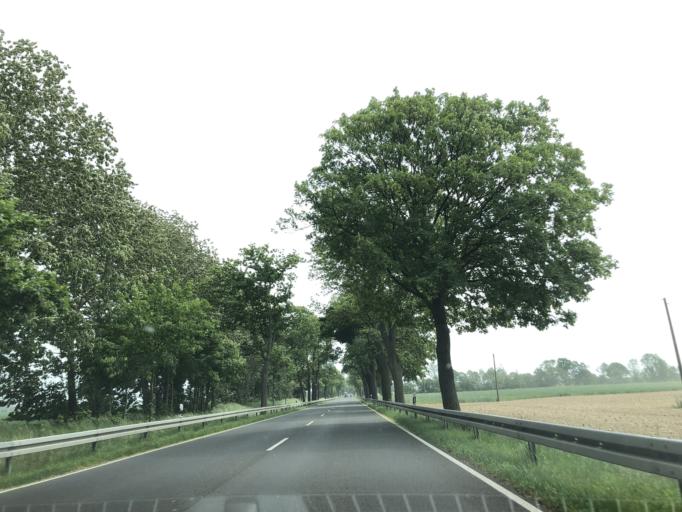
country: DE
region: Brandenburg
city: Gumtow
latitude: 52.9670
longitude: 12.3196
